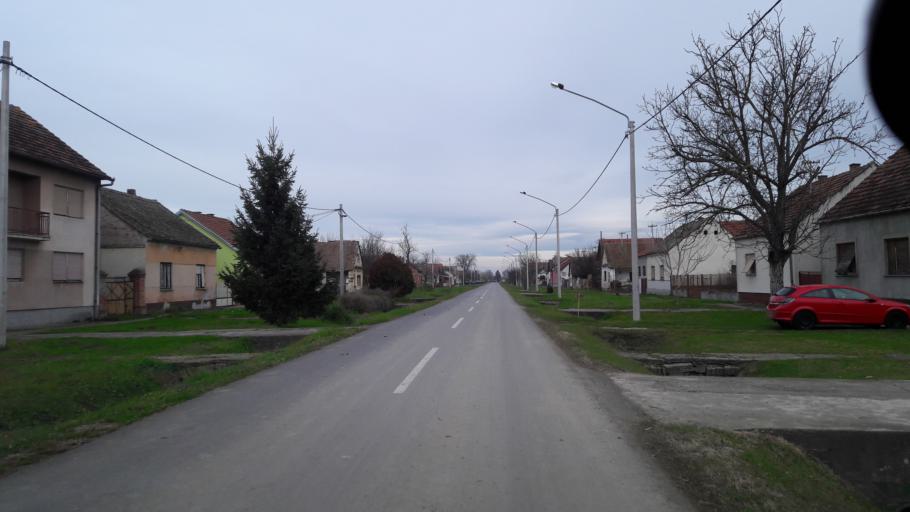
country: HR
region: Osjecko-Baranjska
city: Vladislavci
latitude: 45.4461
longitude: 18.5617
